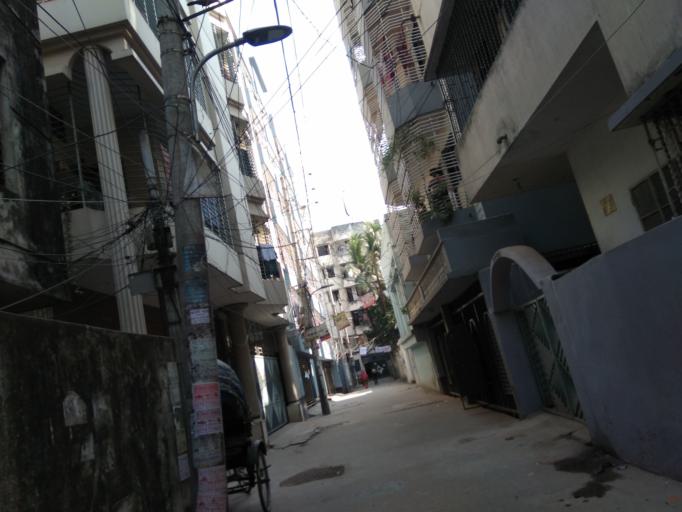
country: BD
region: Dhaka
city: Azimpur
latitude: 23.7462
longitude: 90.3865
